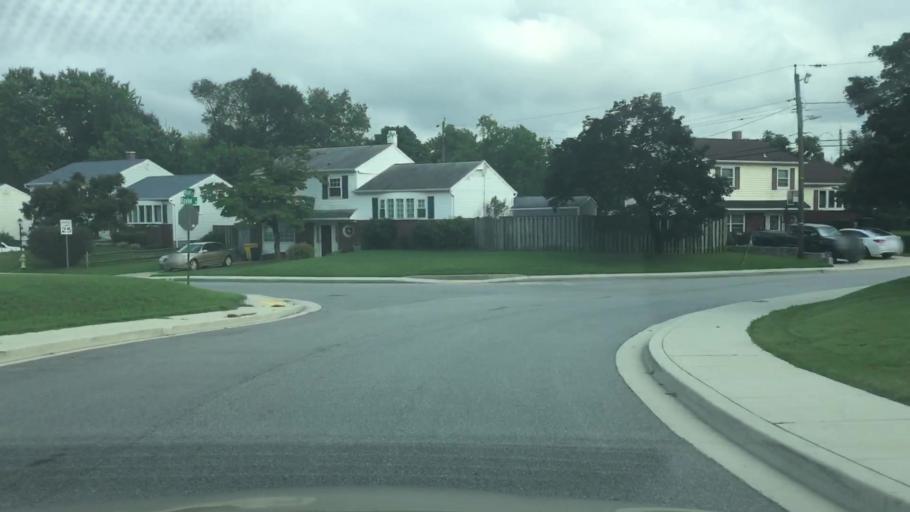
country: US
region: Maryland
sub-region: Anne Arundel County
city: South Gate
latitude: 39.1449
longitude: -76.6416
